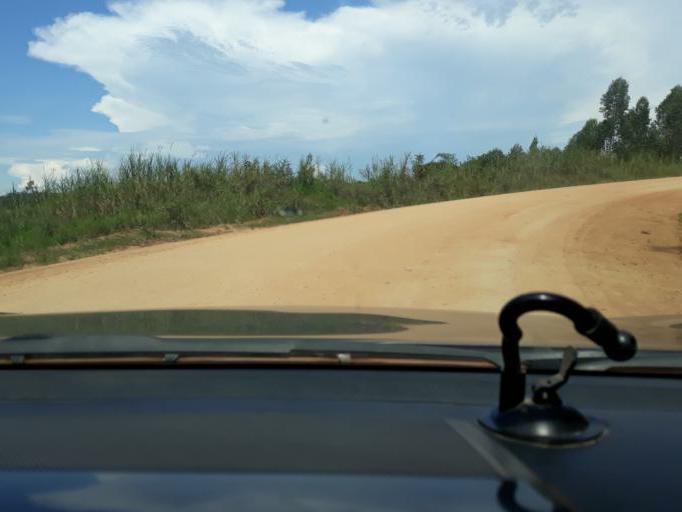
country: CD
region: Eastern Province
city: Bunia
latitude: 1.6317
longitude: 30.2676
